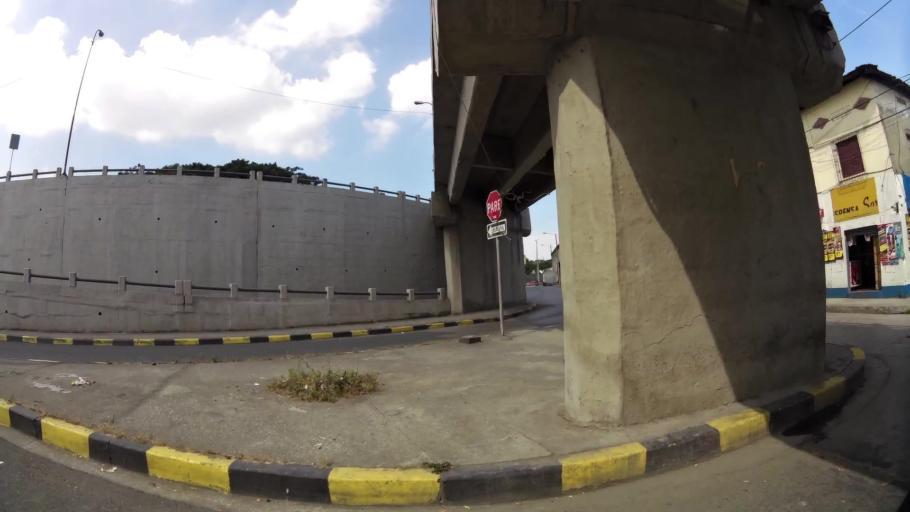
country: EC
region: Guayas
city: Guayaquil
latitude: -2.1415
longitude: -79.9356
